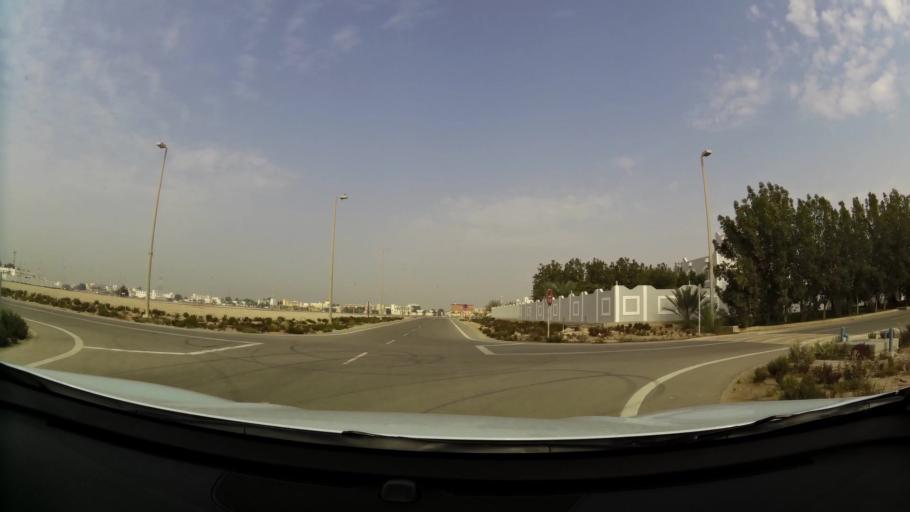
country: AE
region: Abu Dhabi
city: Abu Dhabi
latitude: 24.6566
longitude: 54.7657
